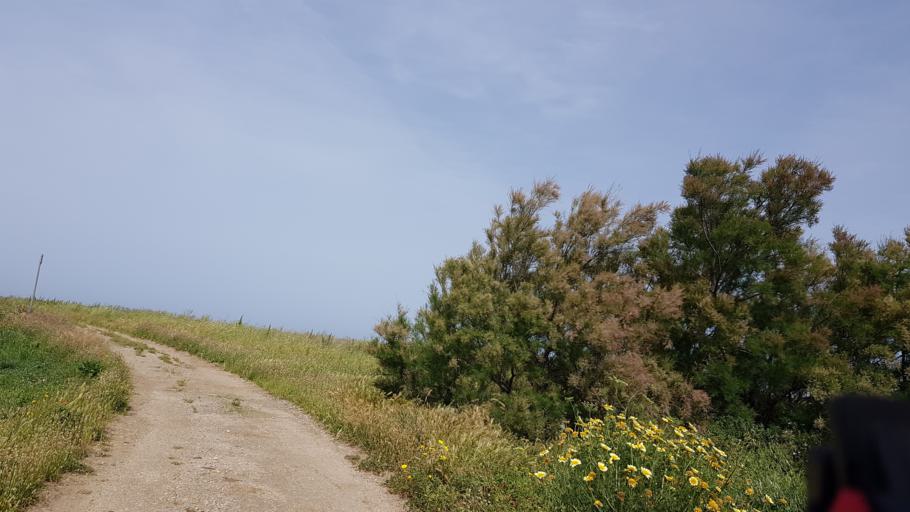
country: IT
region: Apulia
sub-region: Provincia di Brindisi
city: La Rosa
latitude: 40.5891
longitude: 18.0389
